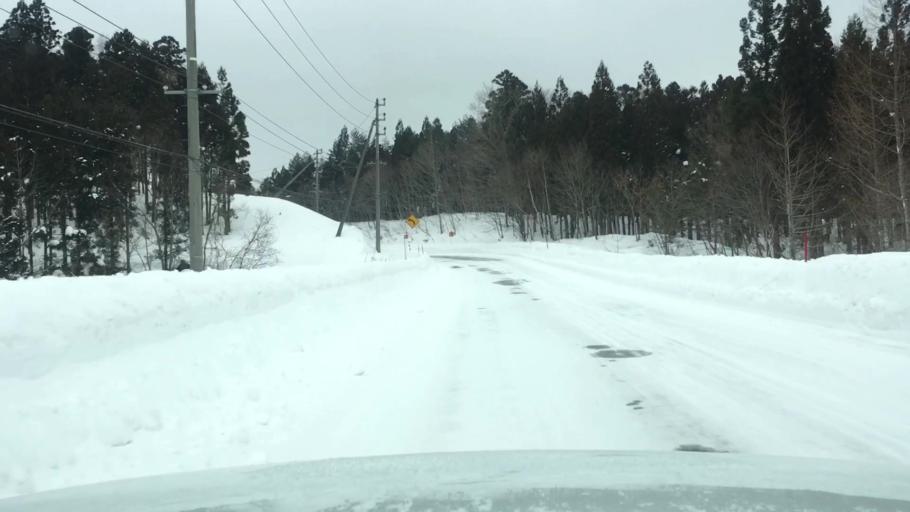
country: JP
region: Akita
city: Hanawa
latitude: 39.9985
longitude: 140.9897
